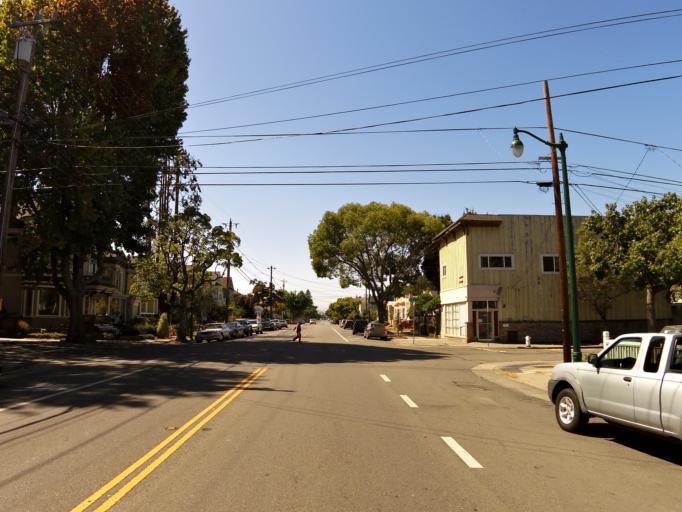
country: US
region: California
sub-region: Alameda County
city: Alameda
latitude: 37.7729
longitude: -122.2606
